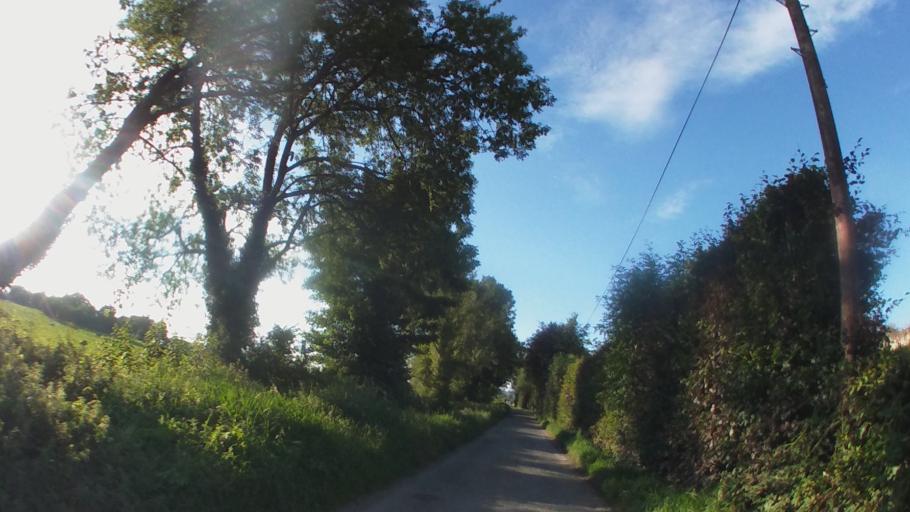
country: IE
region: Leinster
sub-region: Kilkenny
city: Kilkenny
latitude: 52.6907
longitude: -7.1886
